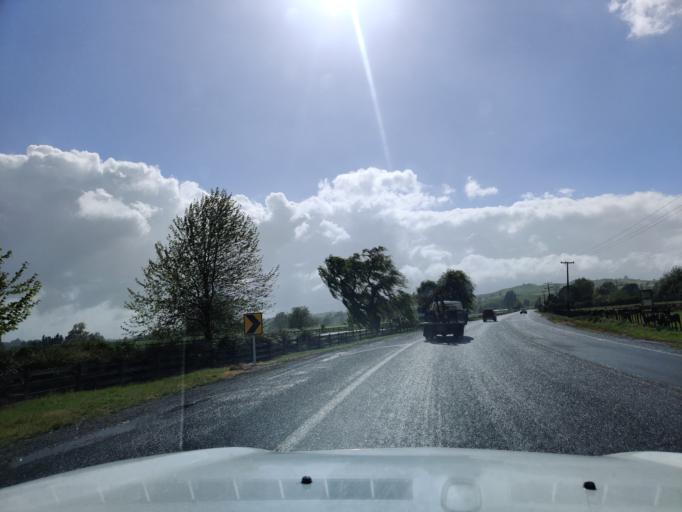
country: NZ
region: Waikato
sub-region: Matamata-Piako District
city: Matamata
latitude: -37.9433
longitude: 175.6601
